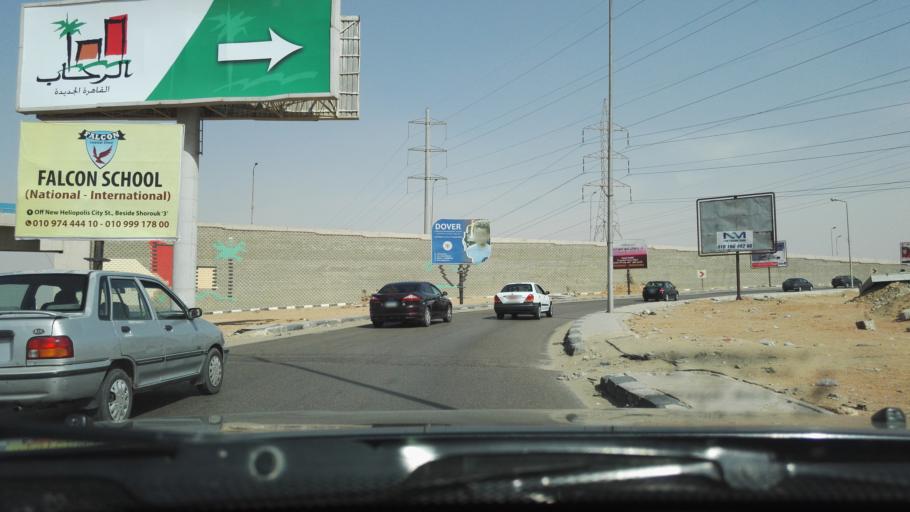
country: EG
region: Muhafazat al Qalyubiyah
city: Al Khankah
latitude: 30.0826
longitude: 31.4700
